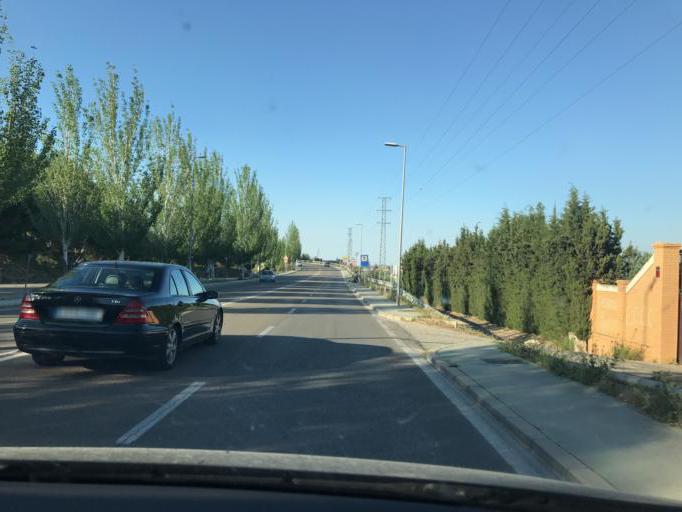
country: ES
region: Andalusia
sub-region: Provincia de Jaen
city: Jaen
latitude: 37.7690
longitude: -3.7729
